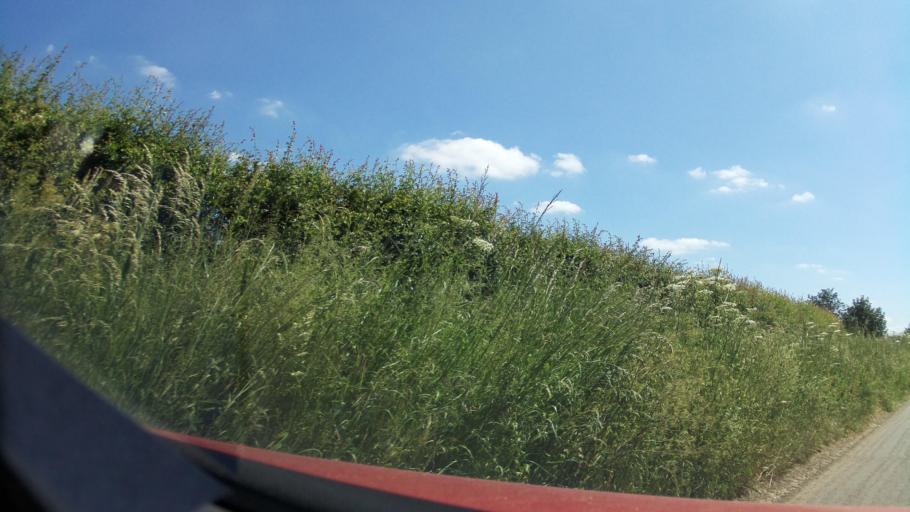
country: GB
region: England
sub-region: Wiltshire
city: Bremhill
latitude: 51.4900
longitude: -2.0441
